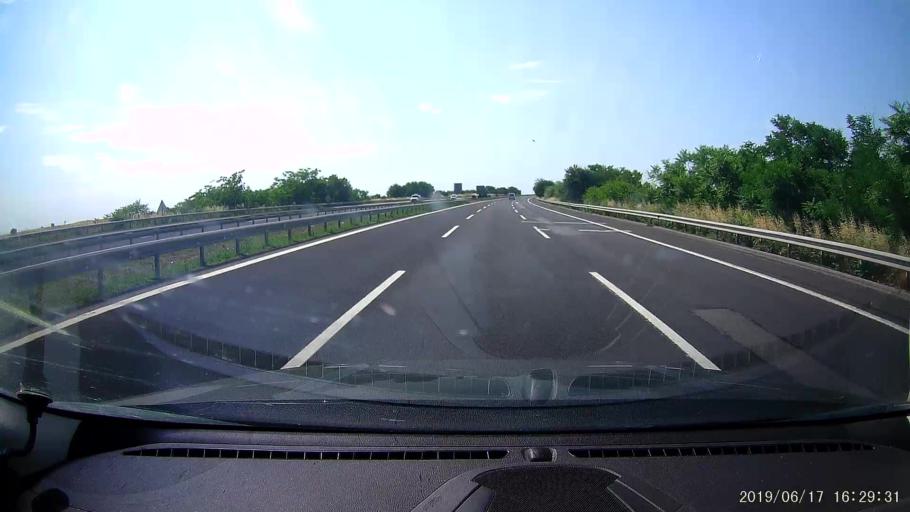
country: TR
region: Tekirdag
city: Beyazkoy
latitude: 41.3345
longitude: 27.6793
